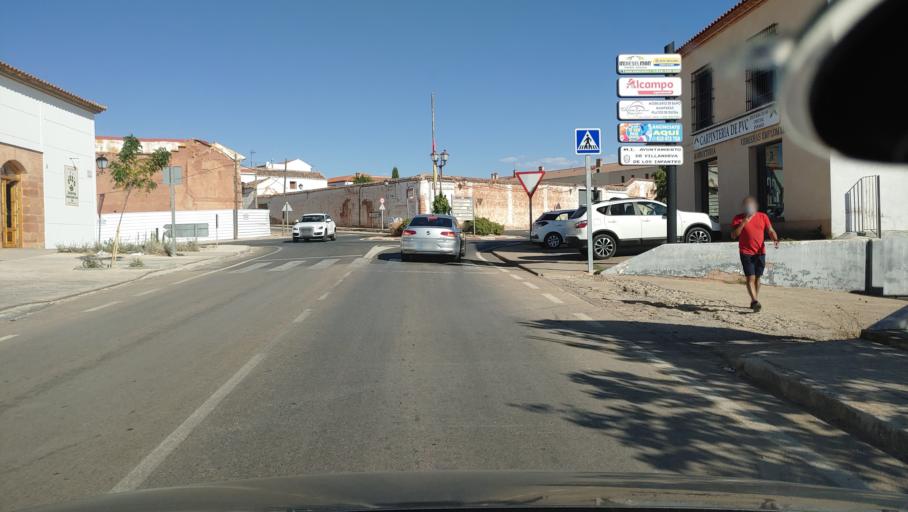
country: ES
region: Castille-La Mancha
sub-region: Provincia de Ciudad Real
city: Infantes
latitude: 38.7368
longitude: -3.0189
